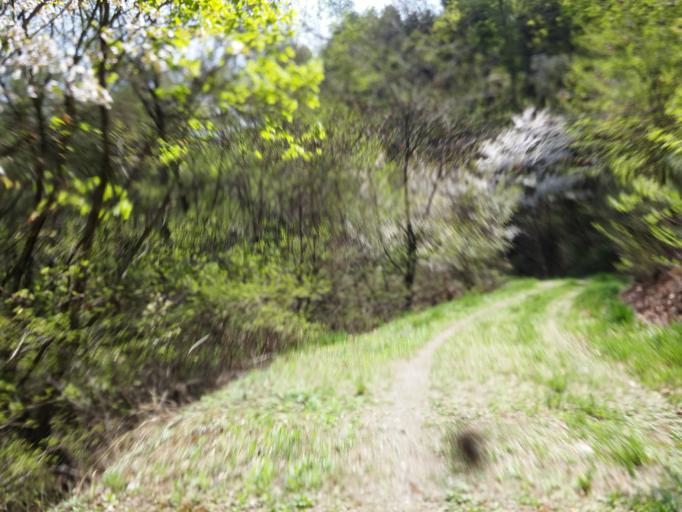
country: KR
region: Daejeon
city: Daejeon
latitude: 36.2760
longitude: 127.4815
